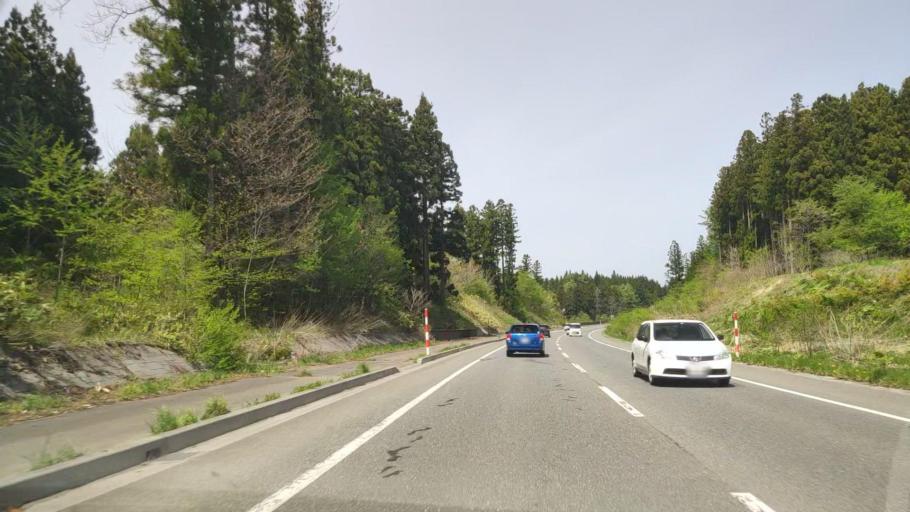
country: JP
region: Aomori
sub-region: Misawa Shi
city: Inuotose
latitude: 40.6879
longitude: 141.1692
